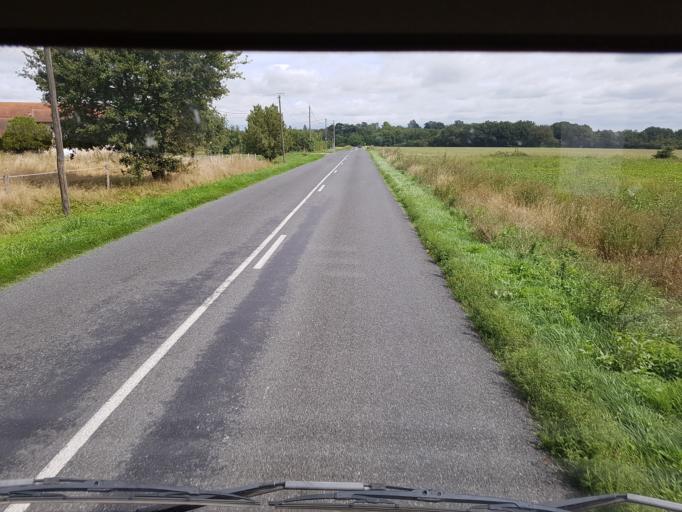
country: FR
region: Rhone-Alpes
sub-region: Departement de l'Ain
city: Beligneux
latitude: 45.9268
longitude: 5.1128
